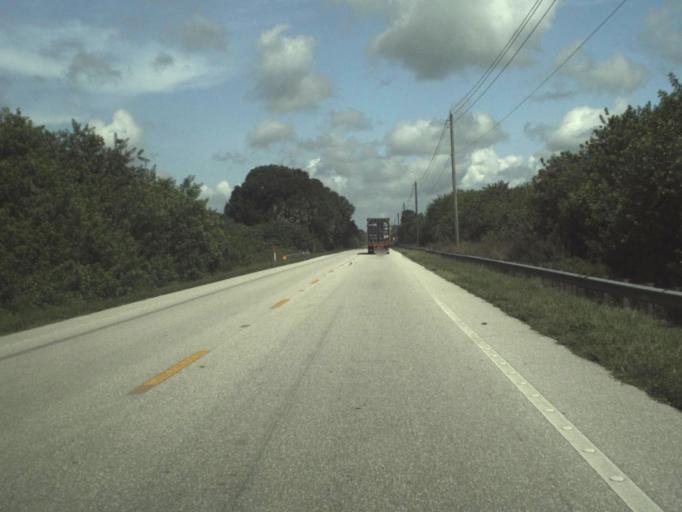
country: US
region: Florida
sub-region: Martin County
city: Indiantown
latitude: 27.0883
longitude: -80.5706
